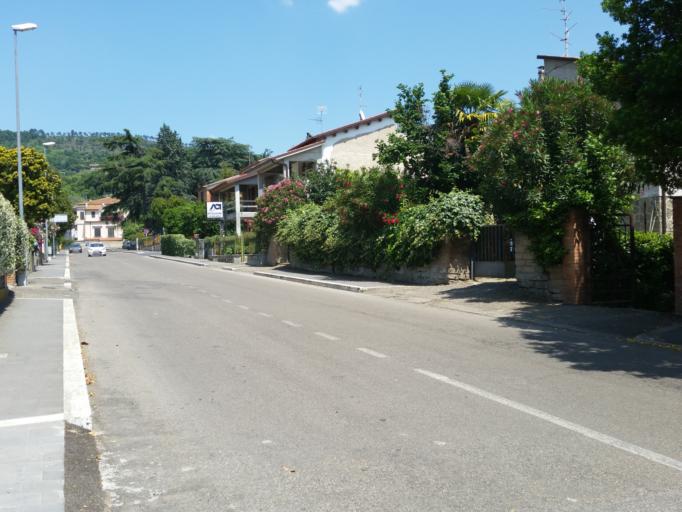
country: IT
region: Latium
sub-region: Provincia di Viterbo
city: Bolsena
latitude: 42.6408
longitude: 11.9878
